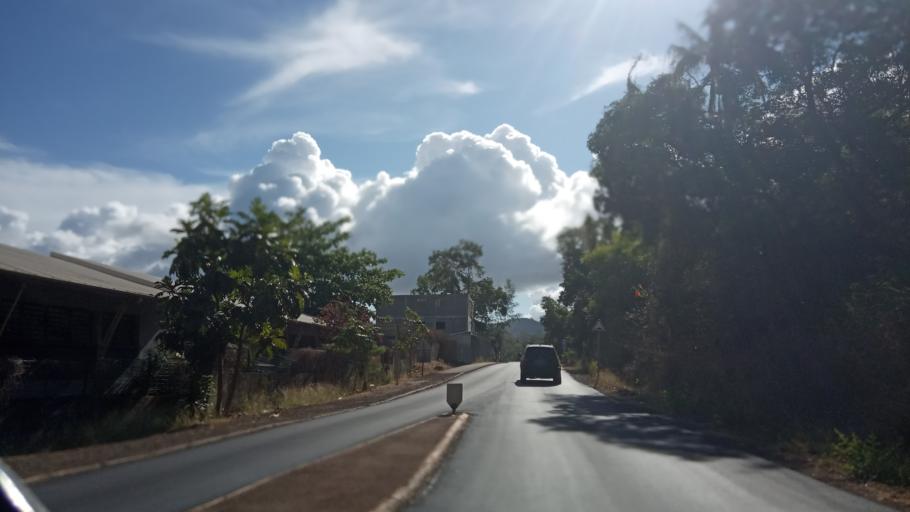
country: YT
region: Bandrele
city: Bandrele
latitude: -12.8921
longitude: 45.2059
